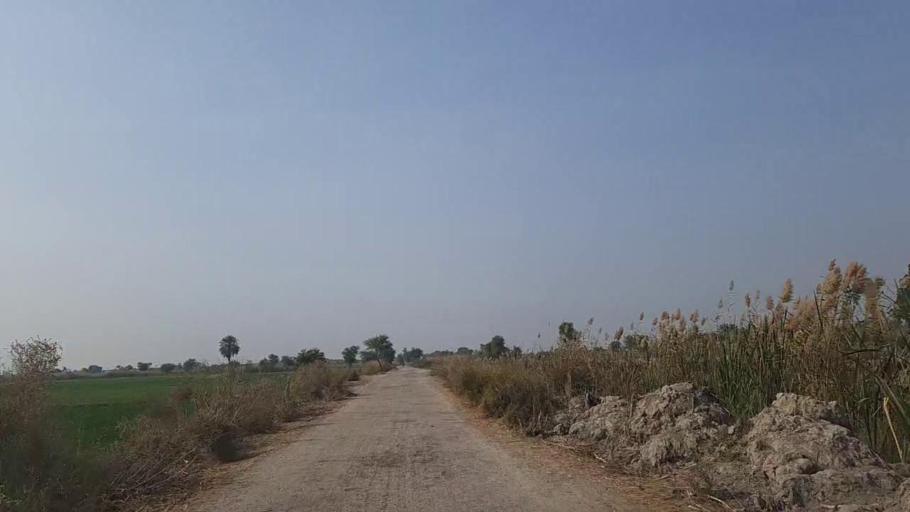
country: PK
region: Sindh
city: Daur
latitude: 26.5051
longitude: 68.4388
